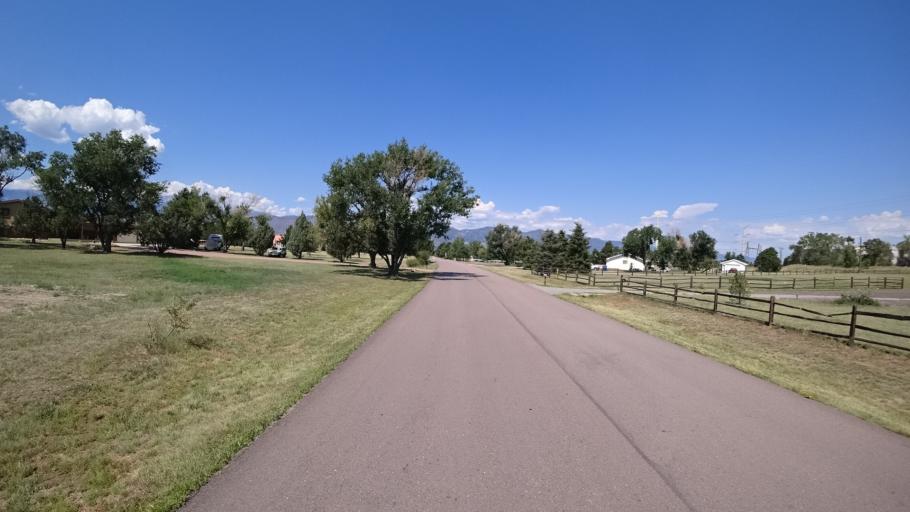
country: US
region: Colorado
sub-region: El Paso County
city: Air Force Academy
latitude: 38.9391
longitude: -104.7795
